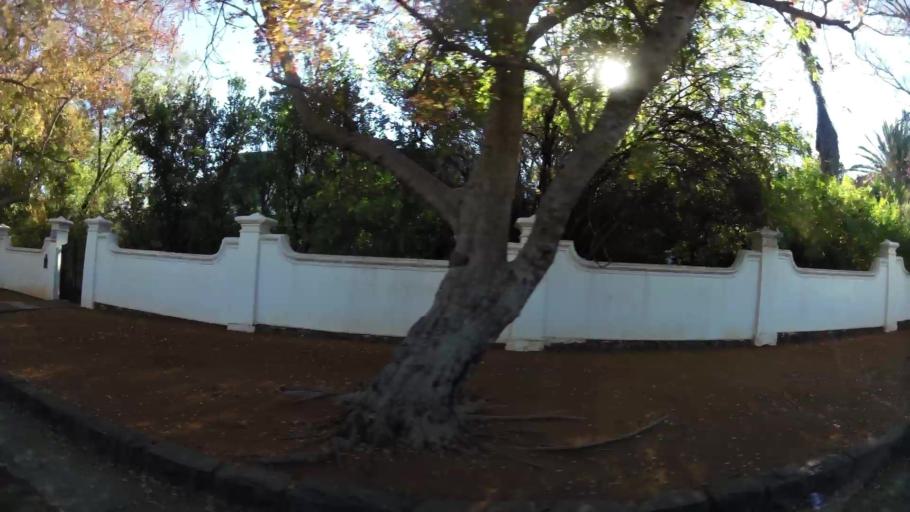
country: ZA
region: Northern Cape
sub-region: Frances Baard District Municipality
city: Kimberley
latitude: -28.7465
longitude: 24.7787
